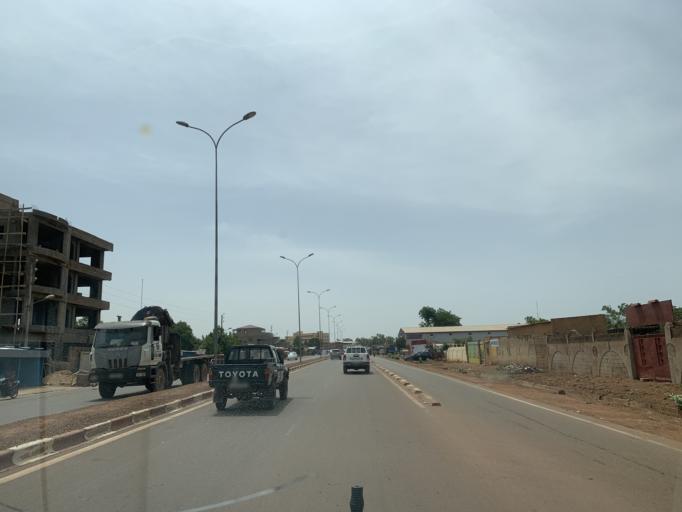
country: BF
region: Centre
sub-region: Kadiogo Province
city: Ouagadougou
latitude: 12.3370
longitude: -1.5075
